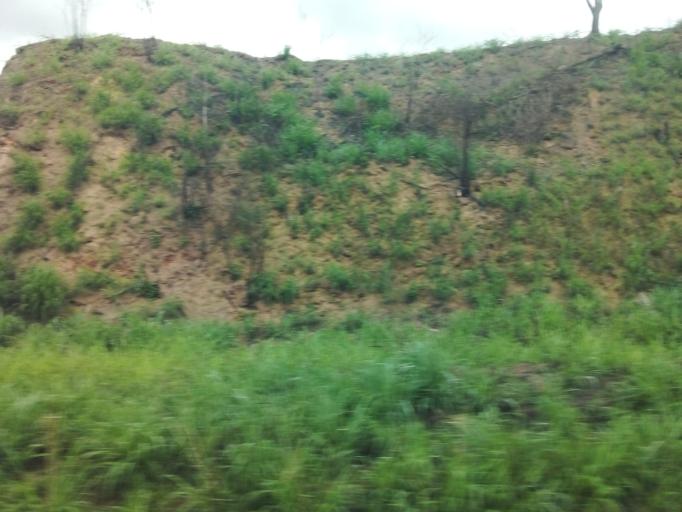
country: BR
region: Minas Gerais
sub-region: Coronel Fabriciano
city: Coronel Fabriciano
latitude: -19.5300
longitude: -42.6717
